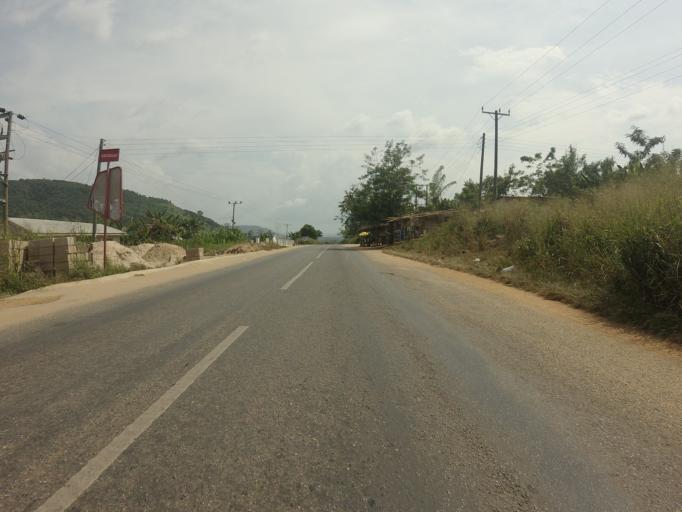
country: GH
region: Eastern
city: Koforidua
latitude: 6.0314
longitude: -0.2567
